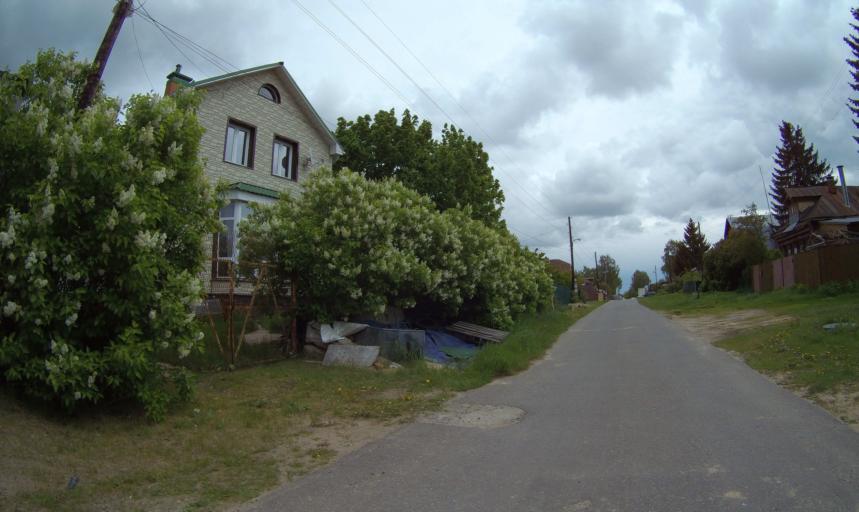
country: RU
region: Moskovskaya
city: Raduzhnyy
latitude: 55.1183
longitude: 38.7615
